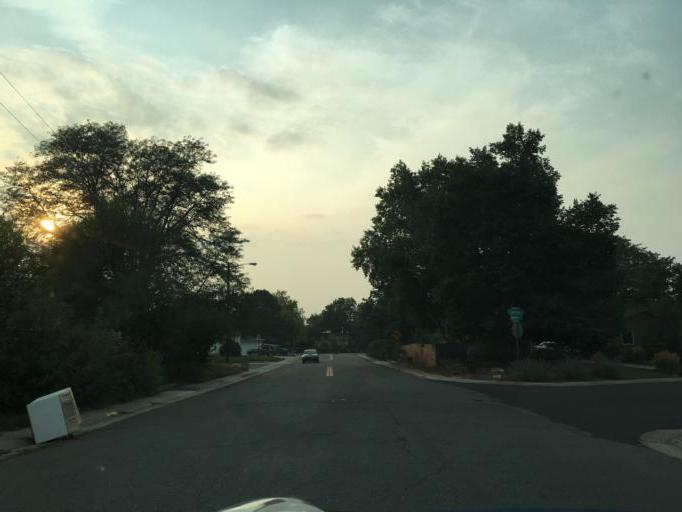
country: US
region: Colorado
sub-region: Arapahoe County
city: Glendale
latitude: 39.6850
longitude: -104.9261
